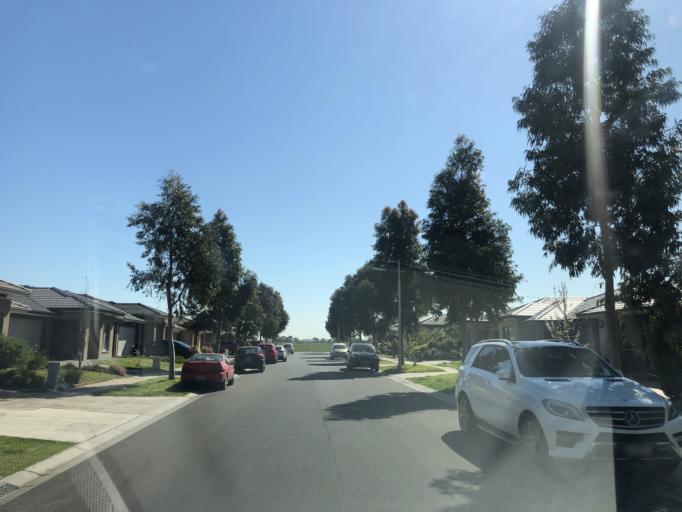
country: AU
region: Victoria
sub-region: Wyndham
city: Hoppers Crossing
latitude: -37.9010
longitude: 144.7176
